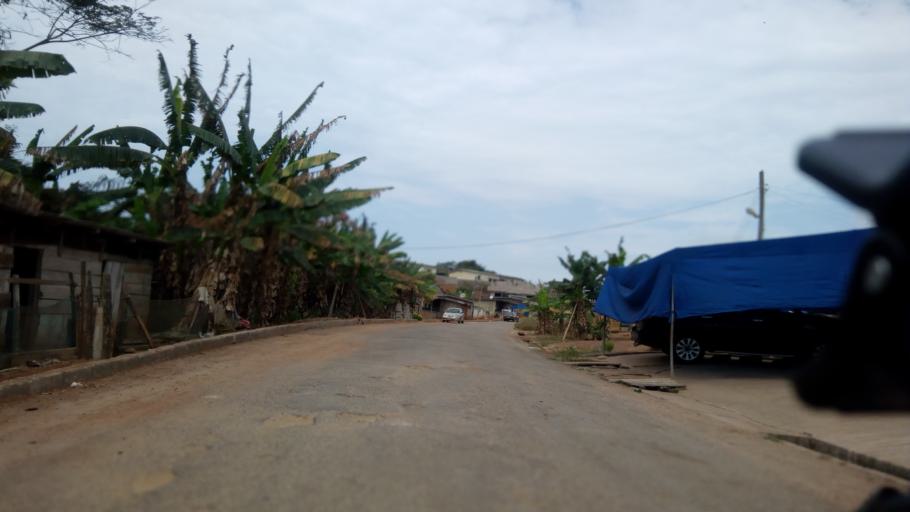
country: GH
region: Central
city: Cape Coast
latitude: 5.1074
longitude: -1.2752
